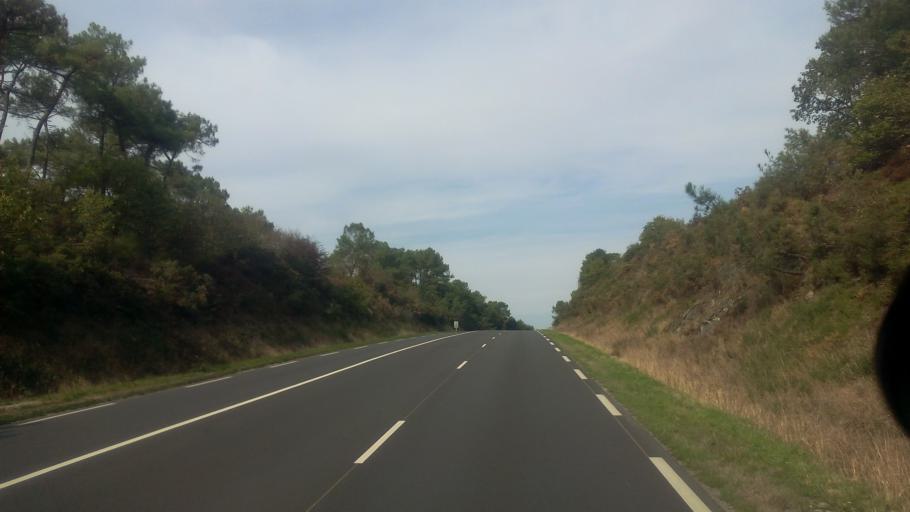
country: FR
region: Brittany
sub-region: Departement du Morbihan
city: Saint-Perreux
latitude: 47.6803
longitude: -2.0848
